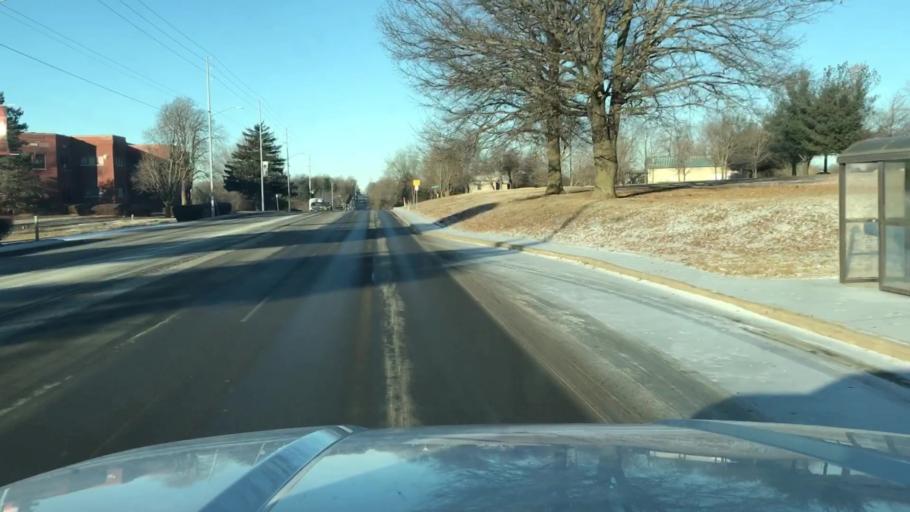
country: US
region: Missouri
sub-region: Buchanan County
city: Saint Joseph
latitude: 39.7770
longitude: -94.8110
